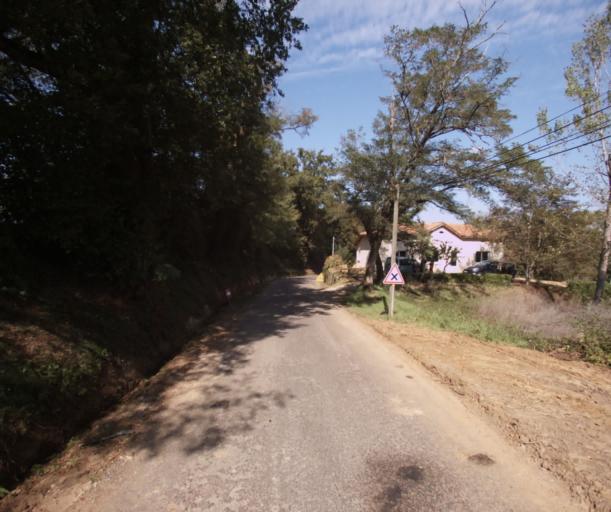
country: FR
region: Midi-Pyrenees
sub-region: Departement du Gers
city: Cazaubon
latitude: 43.9415
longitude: -0.0722
